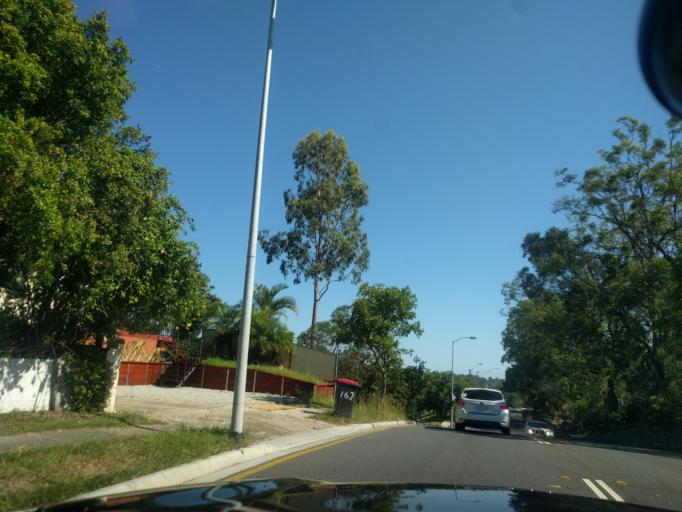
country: AU
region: Queensland
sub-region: Brisbane
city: Stafford Heights
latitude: -27.3999
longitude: 153.0097
